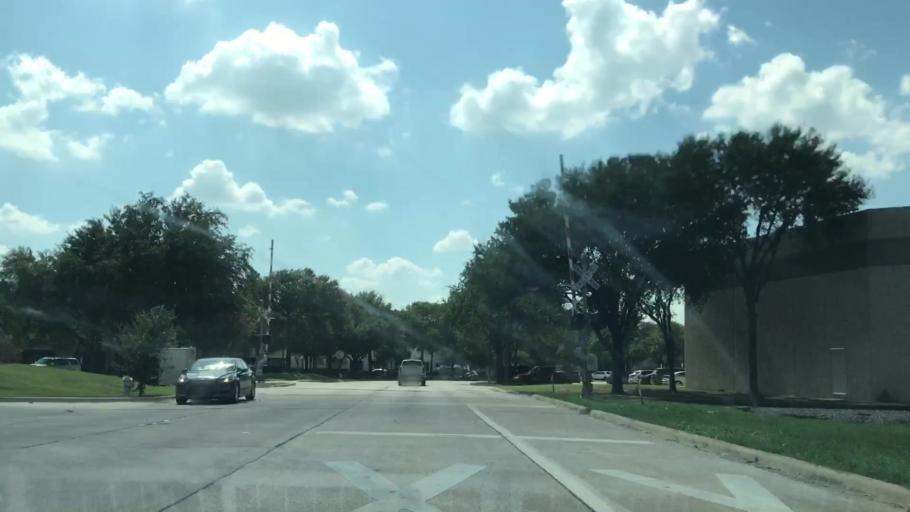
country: US
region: Texas
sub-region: Dallas County
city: Carrollton
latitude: 32.9458
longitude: -96.9187
